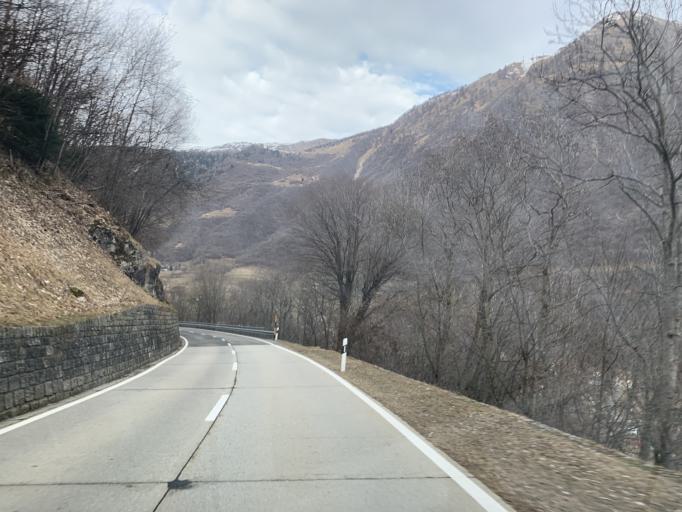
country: CH
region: Ticino
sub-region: Blenio District
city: Cancori
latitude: 46.5239
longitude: 8.9309
